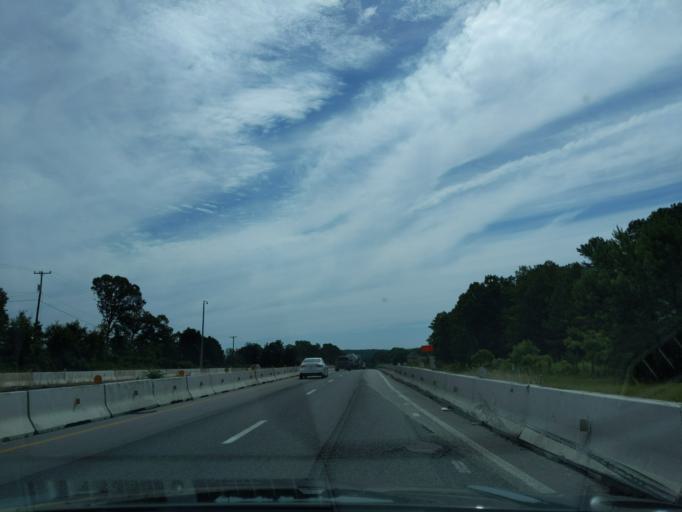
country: US
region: South Carolina
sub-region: Cherokee County
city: East Gaffney
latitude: 35.1098
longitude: -81.6000
